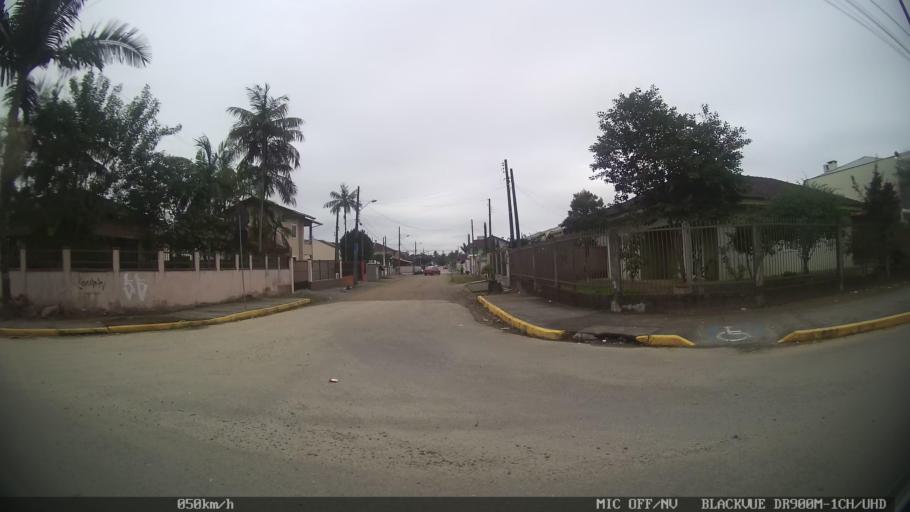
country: BR
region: Santa Catarina
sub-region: Joinville
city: Joinville
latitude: -26.2920
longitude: -48.9119
